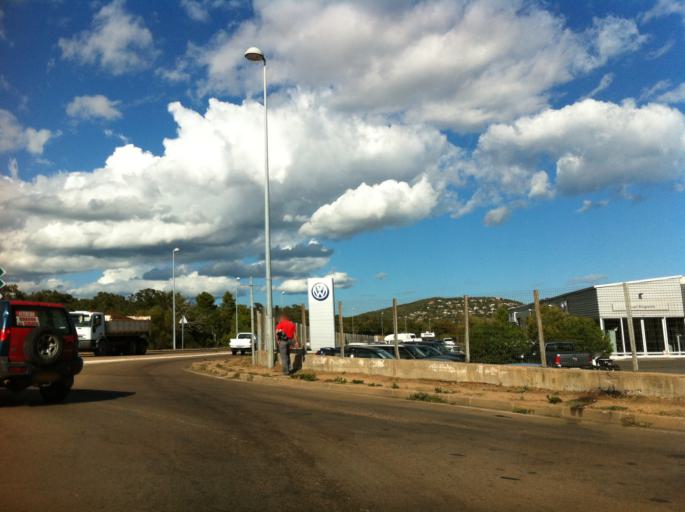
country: FR
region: Corsica
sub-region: Departement de la Corse-du-Sud
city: Porto-Vecchio
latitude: 41.6016
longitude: 9.2689
